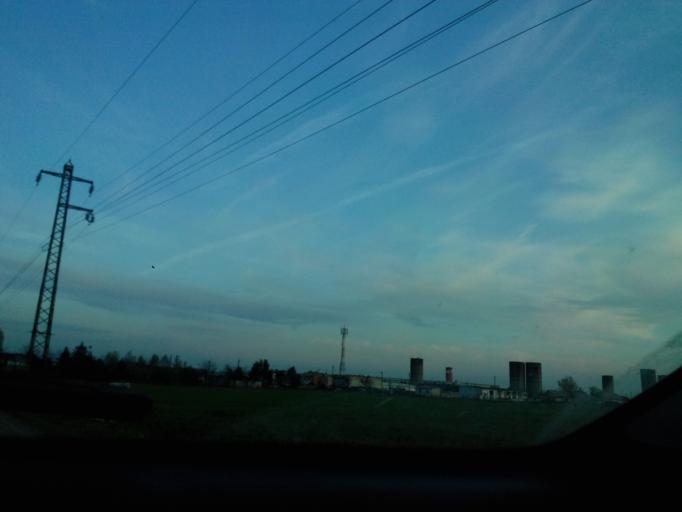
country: RO
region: Prahova
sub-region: Oras Baicoi
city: Baicoi
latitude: 45.0241
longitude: 25.8350
